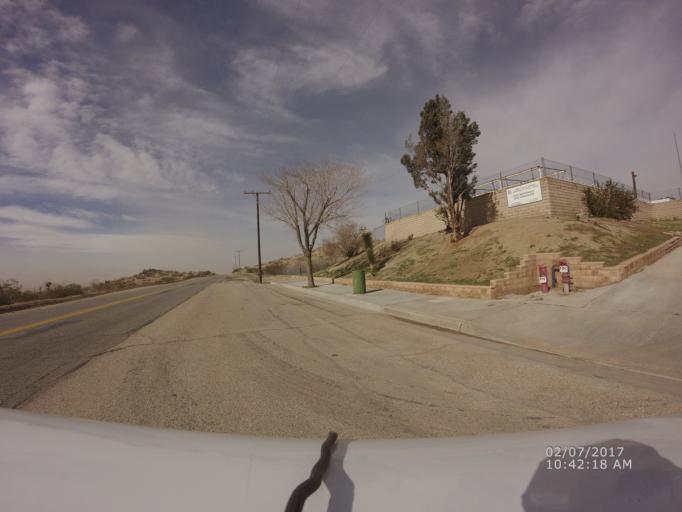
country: US
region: California
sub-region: Los Angeles County
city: Lake Los Angeles
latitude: 34.6900
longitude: -117.8189
